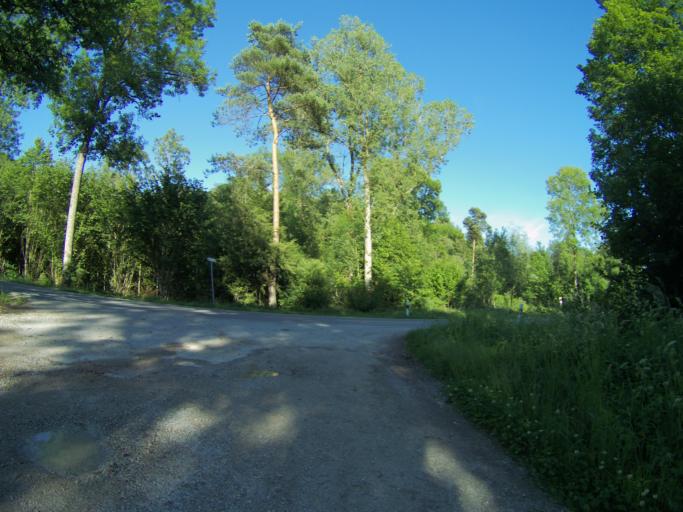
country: DE
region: Bavaria
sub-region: Upper Bavaria
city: Freising
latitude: 48.4161
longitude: 11.7170
